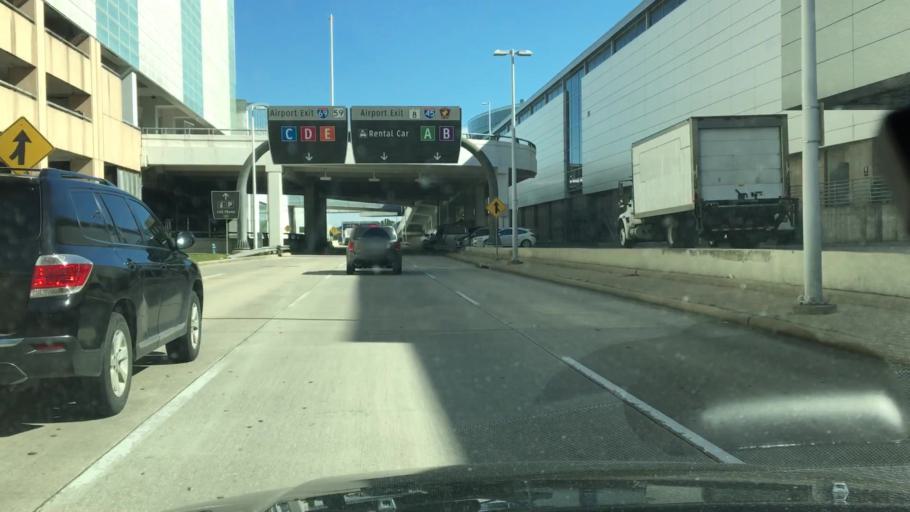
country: US
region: Texas
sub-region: Harris County
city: Aldine
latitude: 29.9860
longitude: -95.3354
